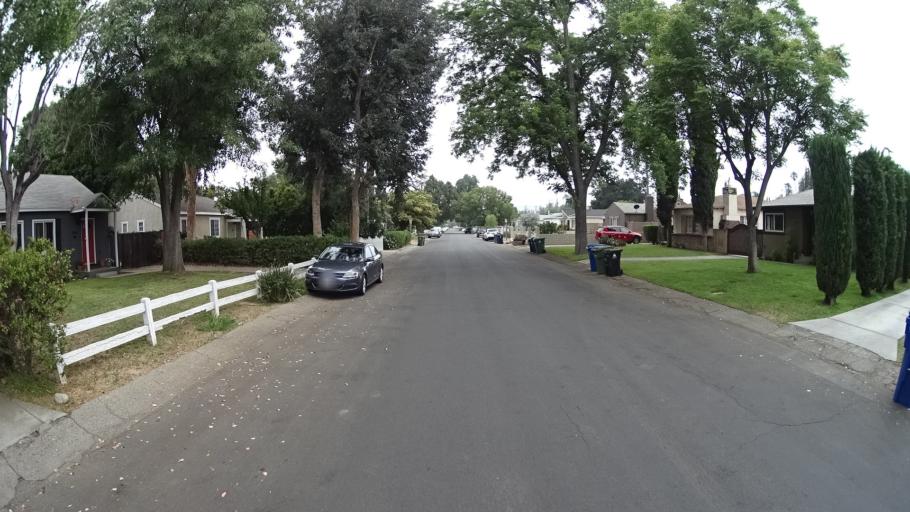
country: US
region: California
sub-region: Los Angeles County
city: Van Nuys
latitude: 34.1771
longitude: -118.4520
